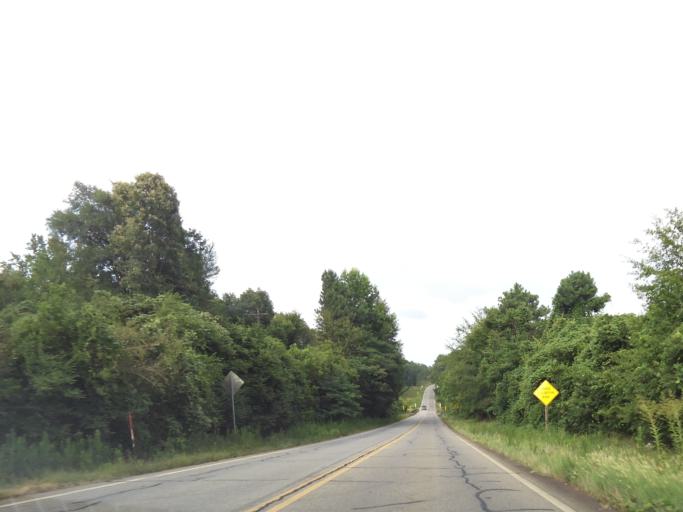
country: US
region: Georgia
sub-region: Bibb County
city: West Point
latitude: 32.8654
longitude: -83.8402
